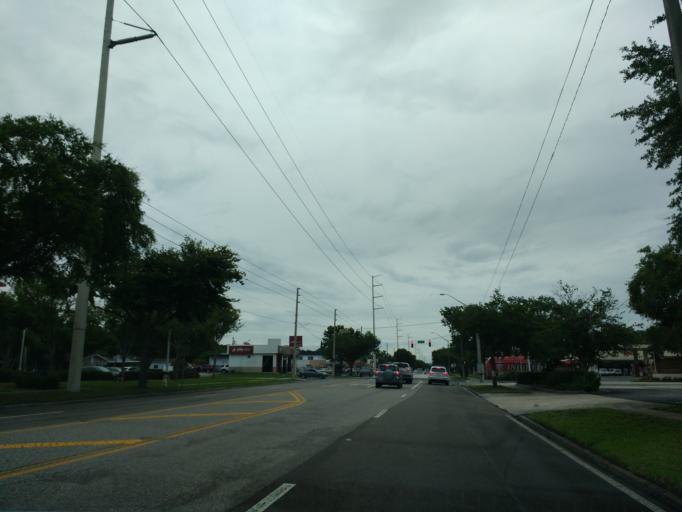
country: US
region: Florida
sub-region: Pinellas County
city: Gulfport
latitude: 27.7709
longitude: -82.7130
